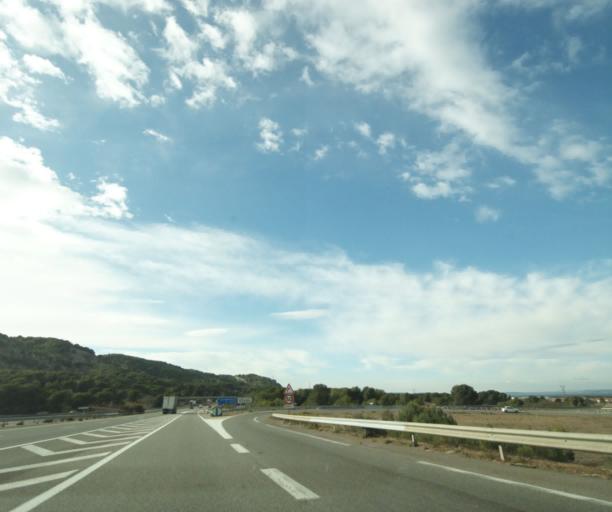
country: FR
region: Provence-Alpes-Cote d'Azur
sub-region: Departement des Bouches-du-Rhone
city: Chateauneuf-les-Martigues
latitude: 43.3734
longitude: 5.1851
